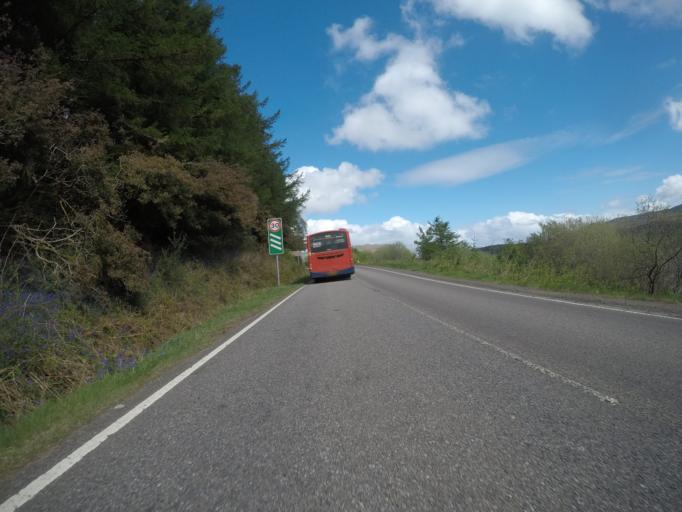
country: GB
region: Scotland
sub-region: Highland
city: Portree
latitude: 57.3980
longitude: -6.2015
